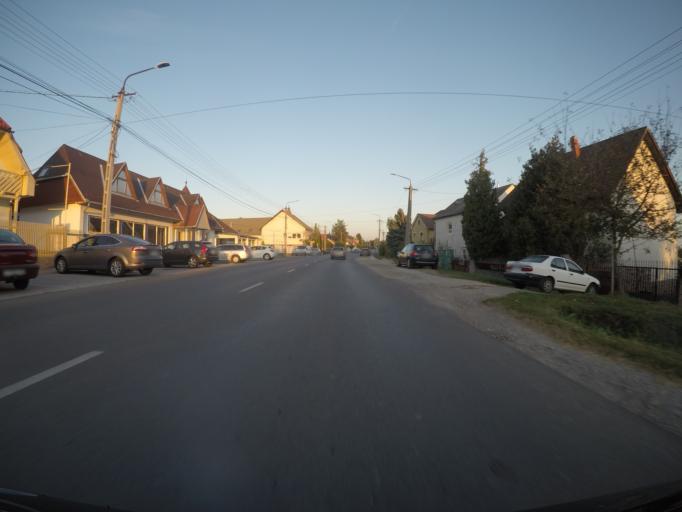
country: HU
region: Baranya
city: Pellerd
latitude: 46.0662
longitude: 18.1775
